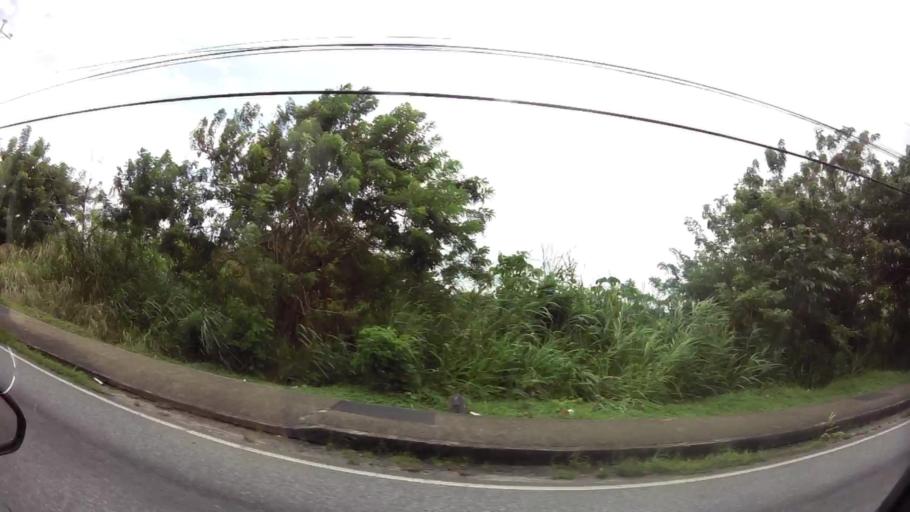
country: TT
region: Tunapuna/Piarco
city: Arouca
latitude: 10.6294
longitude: -61.3175
